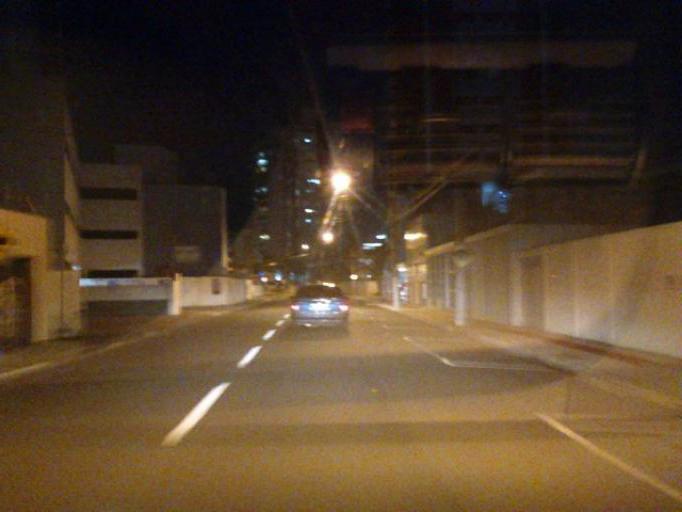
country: BR
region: Santa Catarina
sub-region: Itajai
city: Itajai
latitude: -26.9151
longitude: -48.6551
